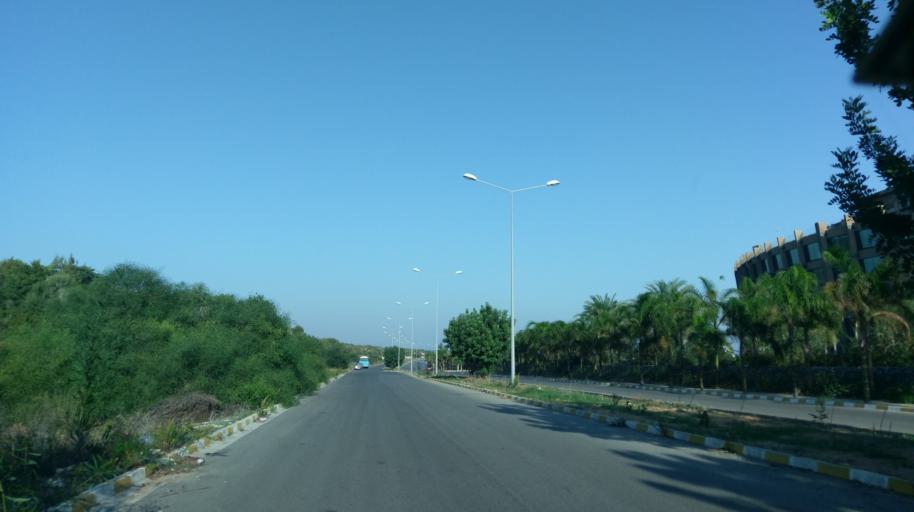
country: CY
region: Ammochostos
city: Leonarisso
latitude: 35.3799
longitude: 34.0885
